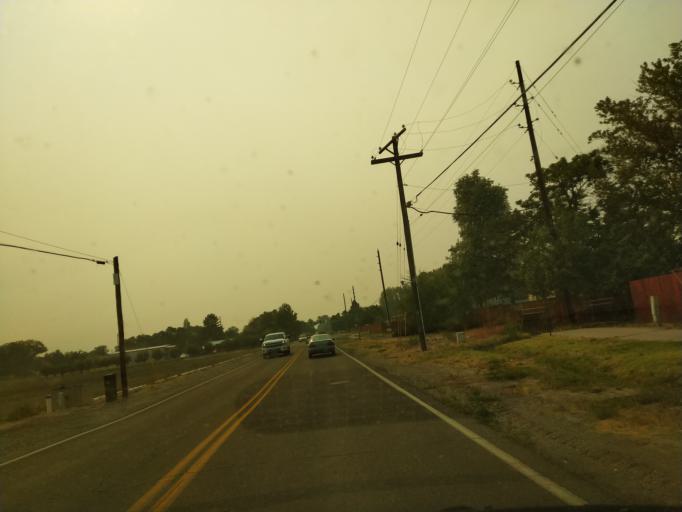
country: US
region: Colorado
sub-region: Mesa County
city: Fruitvale
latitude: 39.0846
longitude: -108.4937
